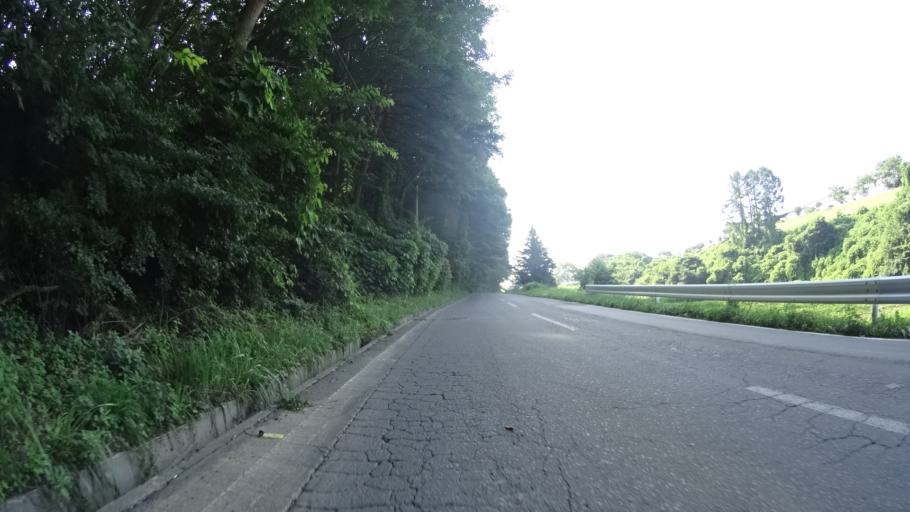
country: JP
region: Nagano
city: Chino
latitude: 35.9733
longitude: 138.1815
